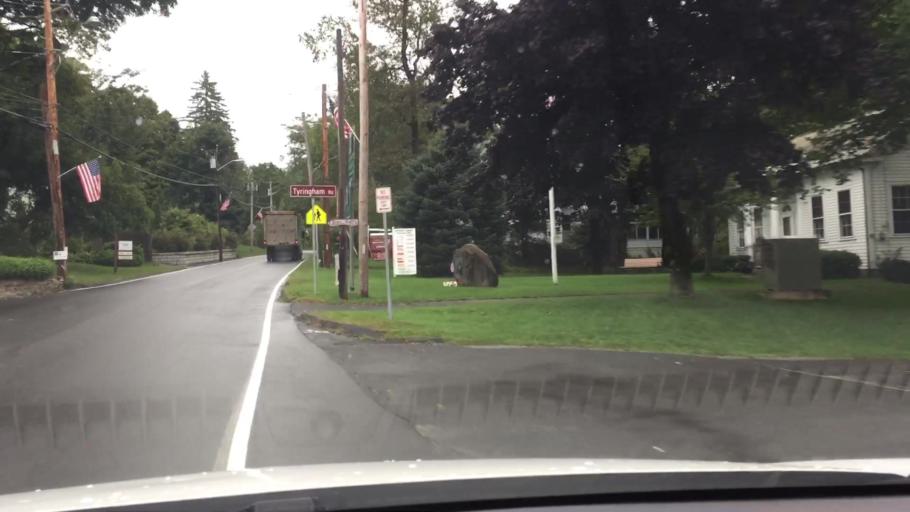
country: US
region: Massachusetts
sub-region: Berkshire County
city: New Marlborough
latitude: 42.1794
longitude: -73.2128
